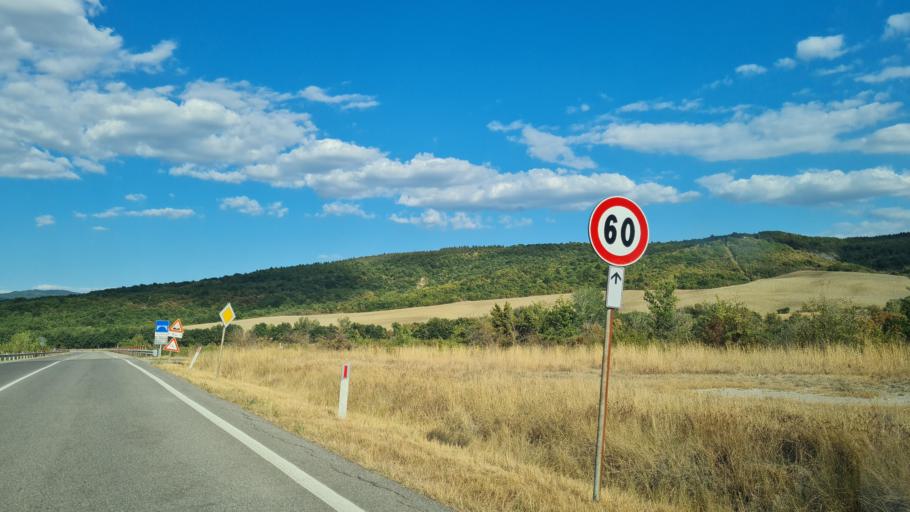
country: IT
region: Tuscany
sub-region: Provincia di Siena
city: Castiglione d'Orcia
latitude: 42.9807
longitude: 11.7068
